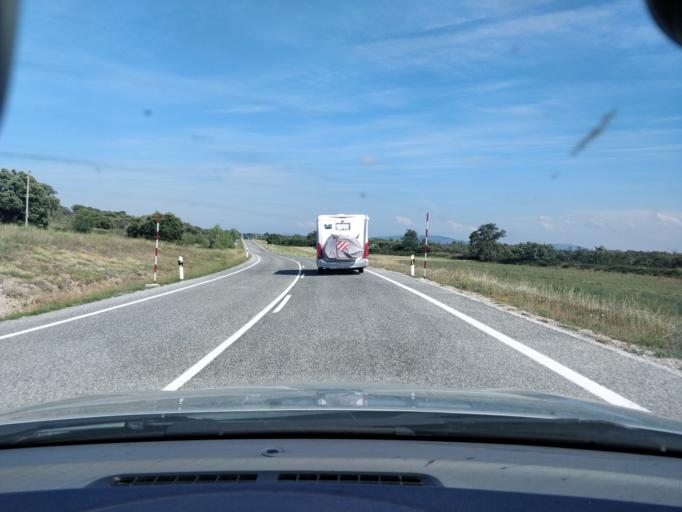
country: ES
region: Cantabria
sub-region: Provincia de Cantabria
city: San Martin de Elines
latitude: 42.9450
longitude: -3.7508
